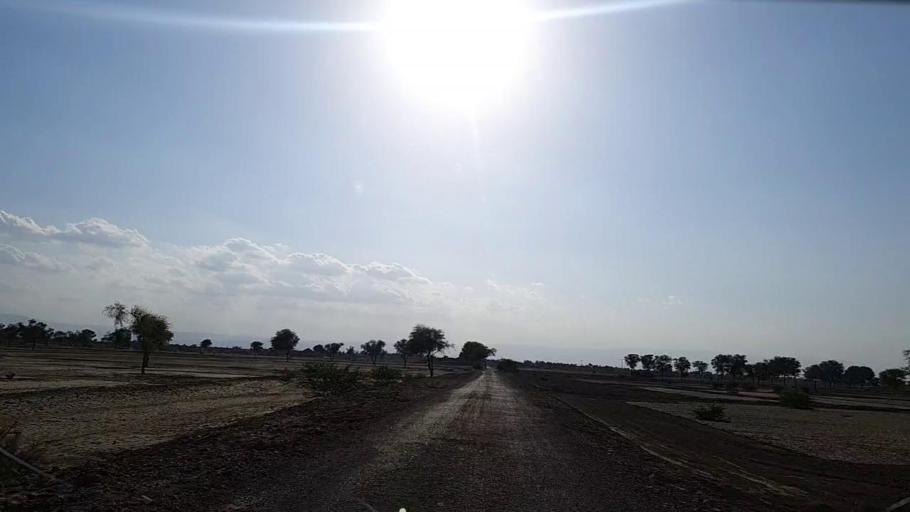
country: PK
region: Sindh
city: Johi
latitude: 26.5842
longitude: 67.5510
